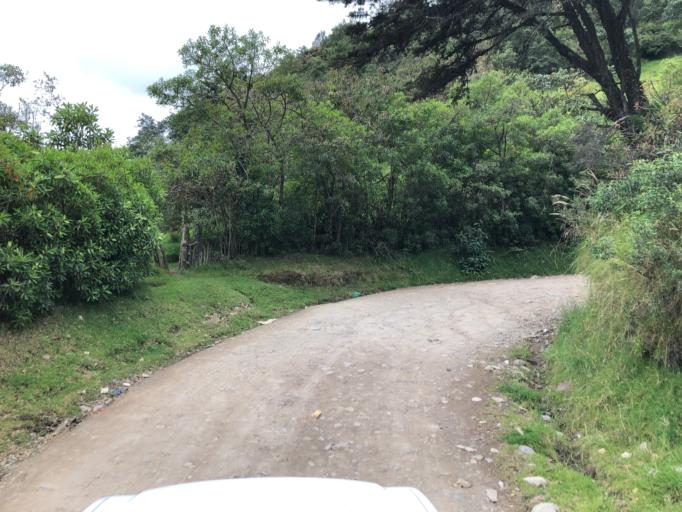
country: CO
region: Cauca
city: Totoro
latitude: 2.5110
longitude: -76.3702
